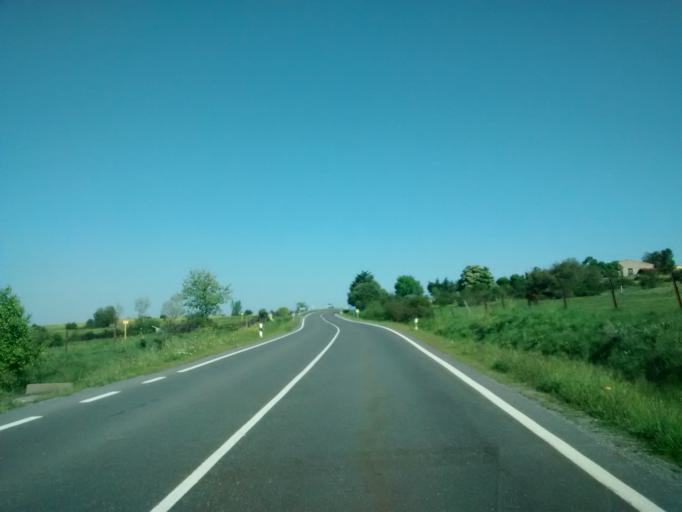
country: ES
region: Castille and Leon
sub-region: Provincia de Segovia
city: San Ildefonso
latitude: 40.9214
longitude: -4.0234
